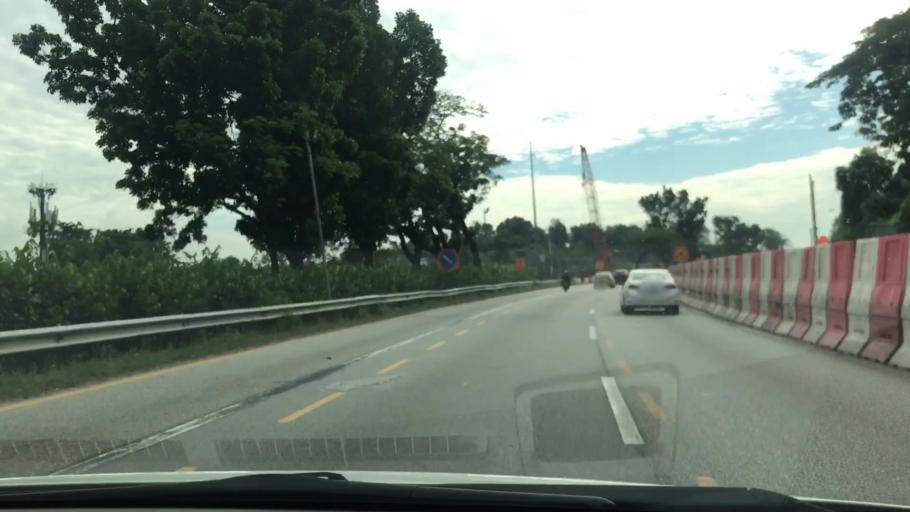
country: MY
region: Kuala Lumpur
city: Kuala Lumpur
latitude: 3.1122
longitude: 101.6864
